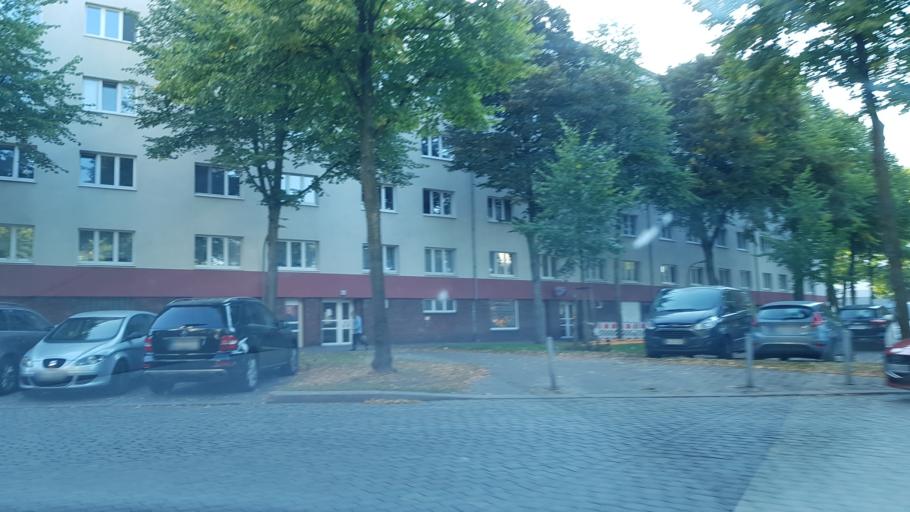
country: DE
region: Hamburg
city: Rothenburgsort
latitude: 53.5384
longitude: 10.0349
